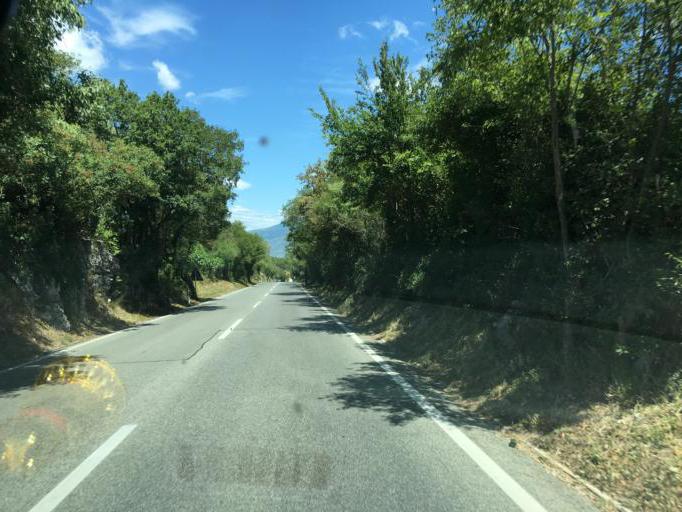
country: HR
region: Istarska
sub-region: Grad Labin
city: Labin
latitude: 45.1418
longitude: 14.1480
